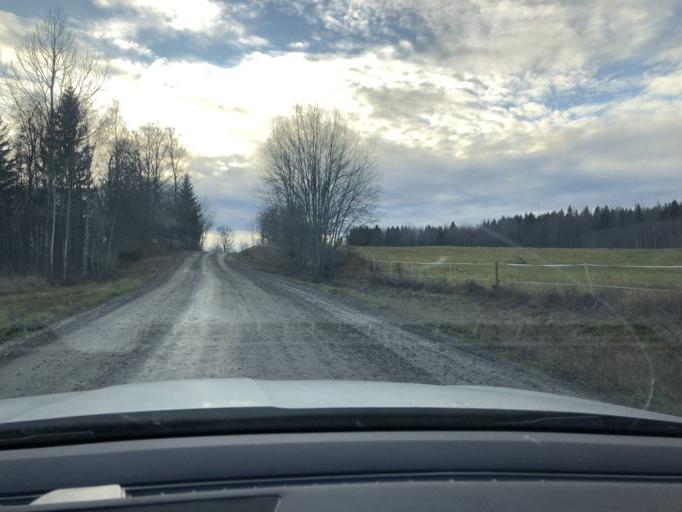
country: SE
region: Gaevleborg
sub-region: Hudiksvalls Kommun
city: Sorforsa
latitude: 61.7321
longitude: 16.9241
